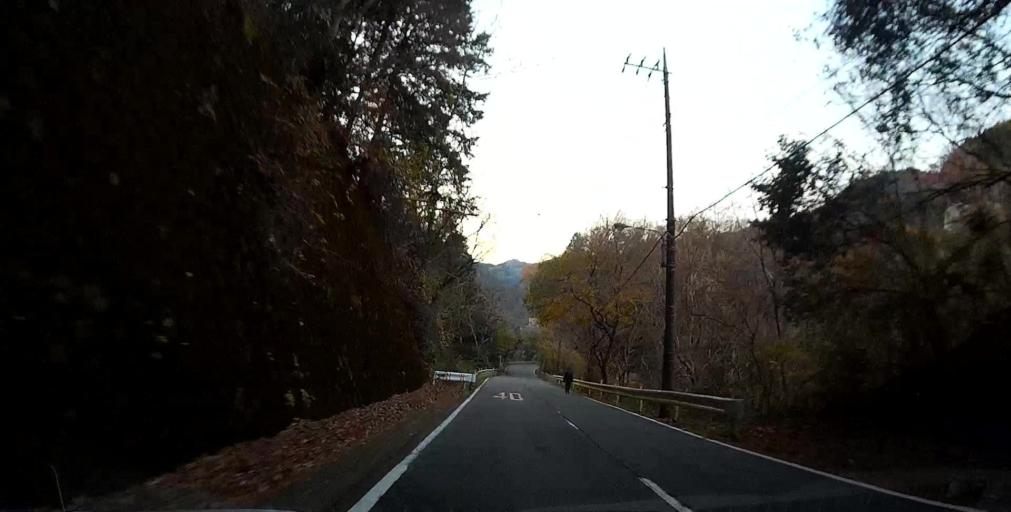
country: JP
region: Yamanashi
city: Uenohara
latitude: 35.5668
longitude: 139.2071
